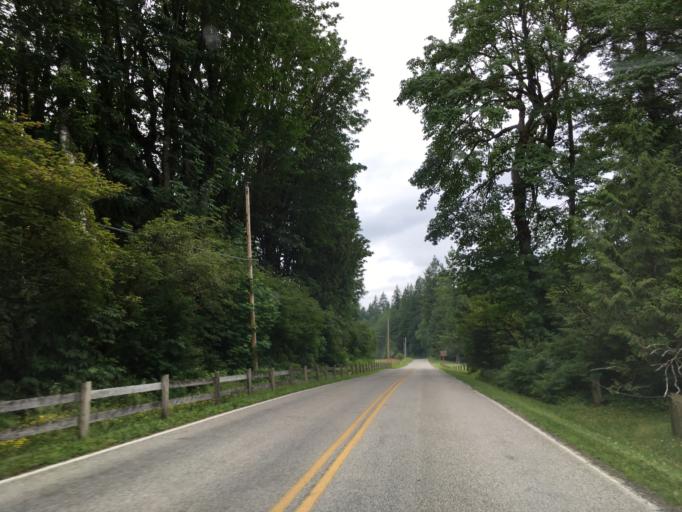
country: US
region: Washington
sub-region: Whatcom County
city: Peaceful Valley
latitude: 48.9661
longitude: -122.0767
